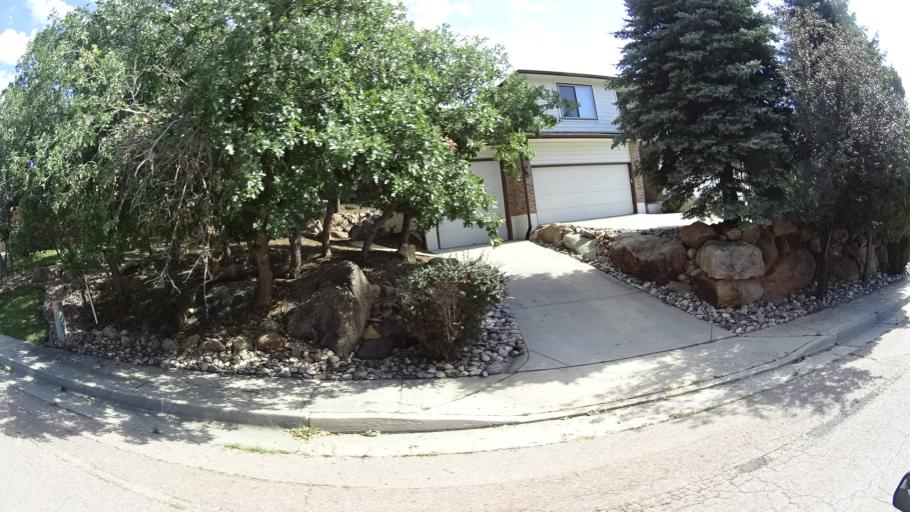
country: US
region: Colorado
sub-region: El Paso County
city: Fort Carson
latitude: 38.7545
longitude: -104.8342
